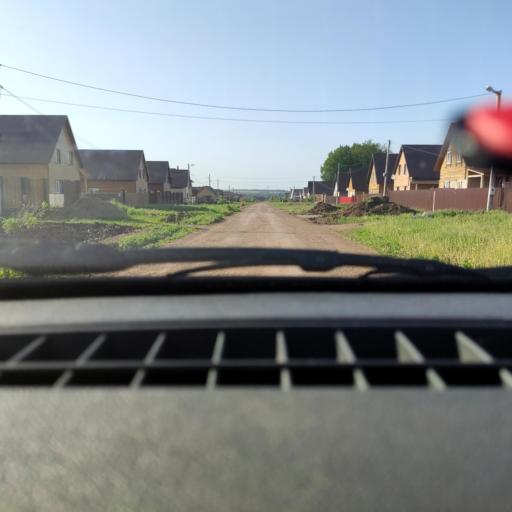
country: RU
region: Bashkortostan
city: Iglino
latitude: 54.8184
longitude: 56.4362
